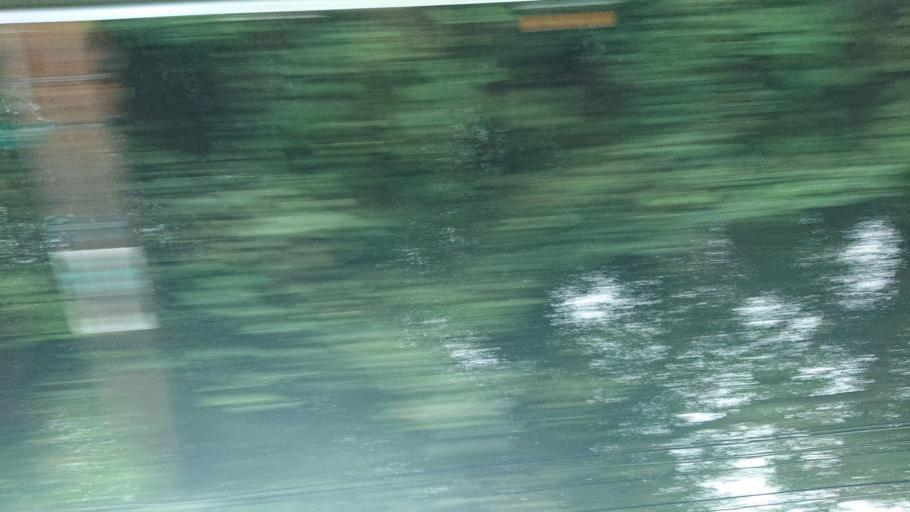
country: TW
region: Taiwan
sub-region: Chiayi
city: Jiayi Shi
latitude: 23.4770
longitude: 120.7135
